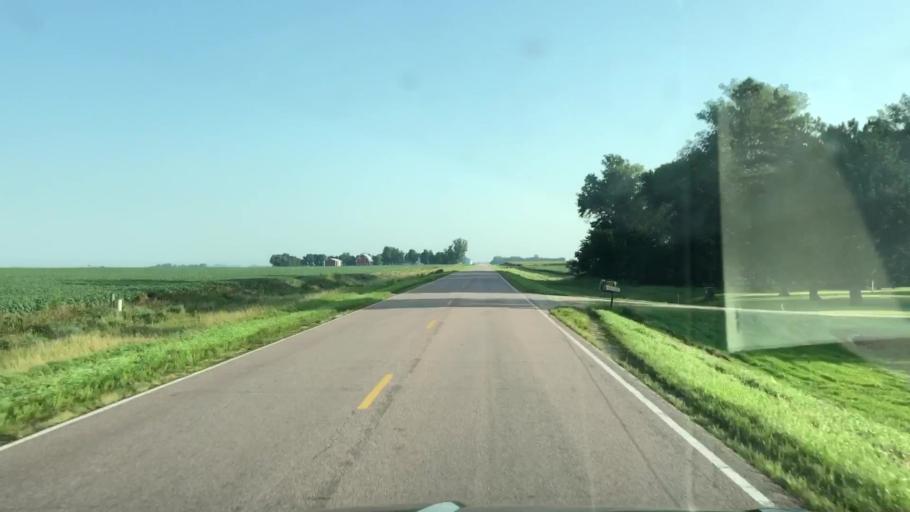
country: US
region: Iowa
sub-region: Lyon County
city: George
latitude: 43.3052
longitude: -95.9992
